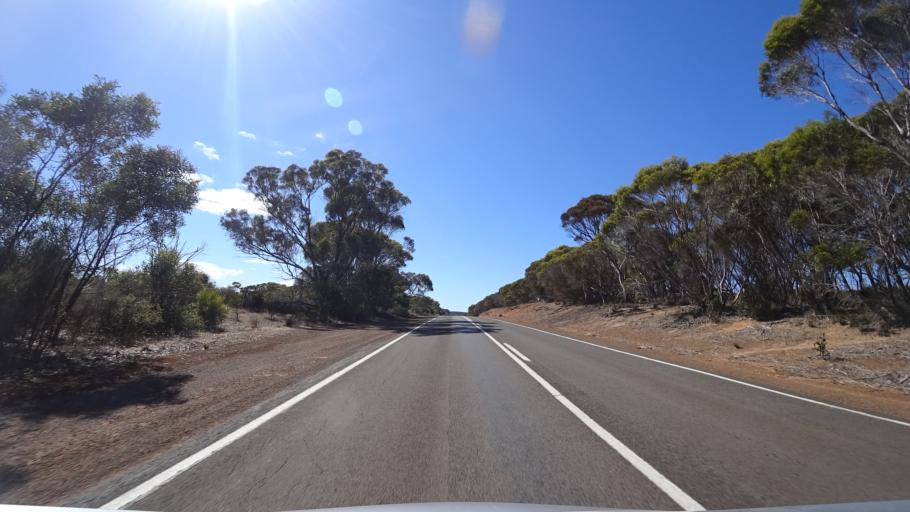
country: AU
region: South Australia
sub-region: Kangaroo Island
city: Kingscote
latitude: -35.7536
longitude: 137.5990
